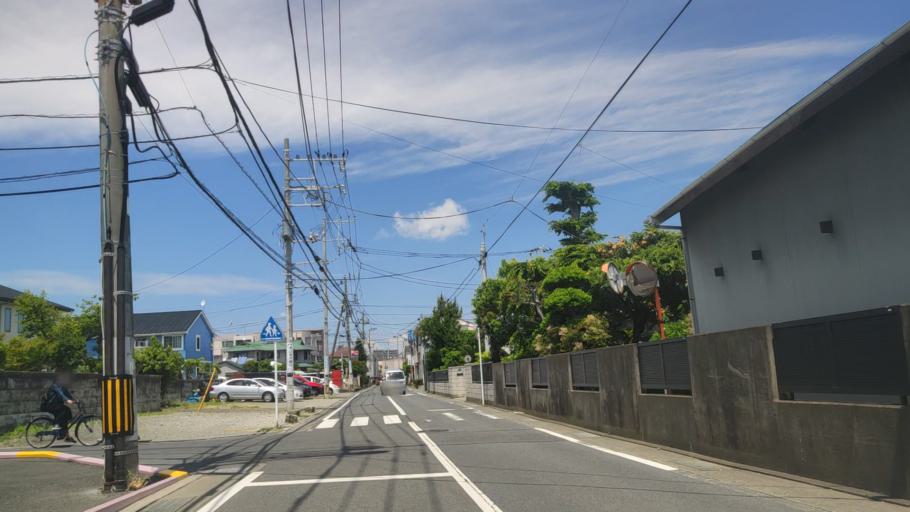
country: JP
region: Kanagawa
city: Chigasaki
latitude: 35.3409
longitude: 139.3976
